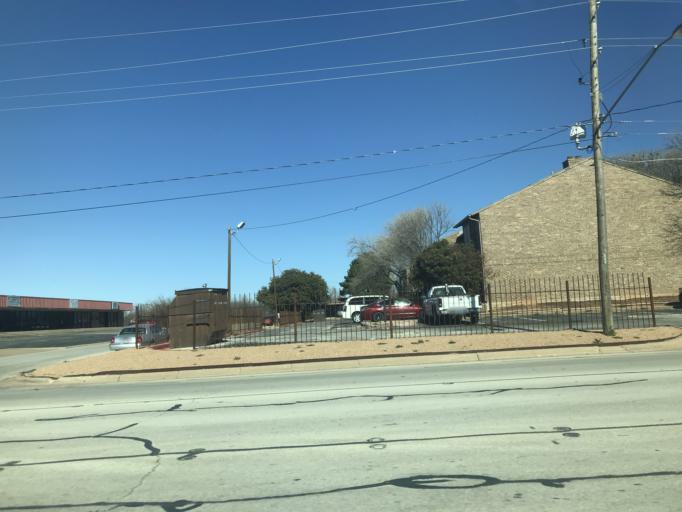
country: US
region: Texas
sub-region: Taylor County
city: Abilene
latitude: 32.4441
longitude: -99.7968
